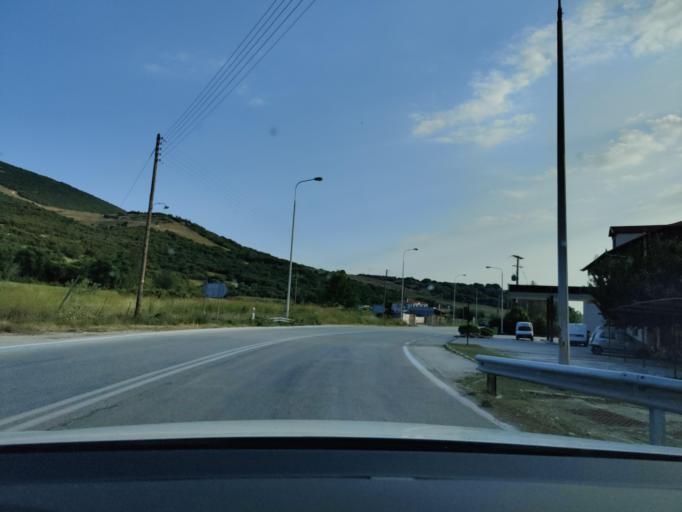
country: GR
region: East Macedonia and Thrace
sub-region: Nomos Kavalas
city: Zygos
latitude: 40.9962
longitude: 24.3832
